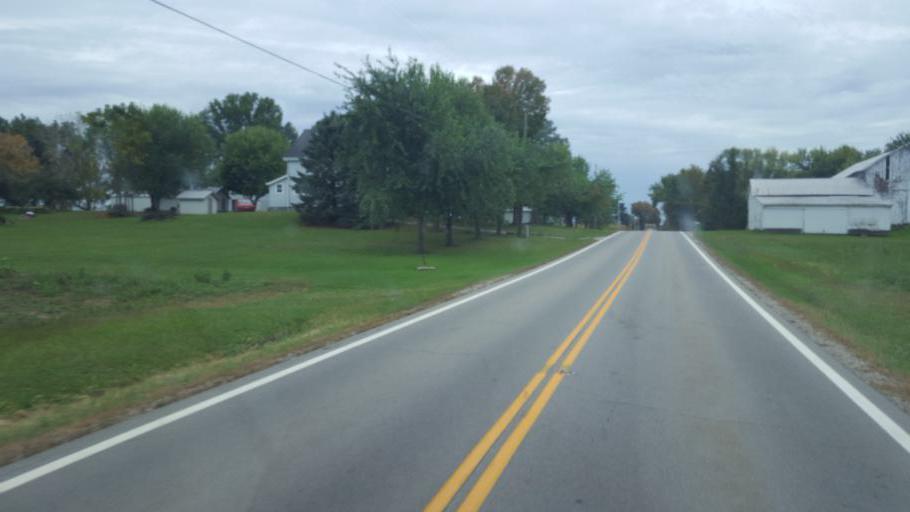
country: US
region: Ohio
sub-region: Huron County
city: Wakeman
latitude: 41.2697
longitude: -82.3954
